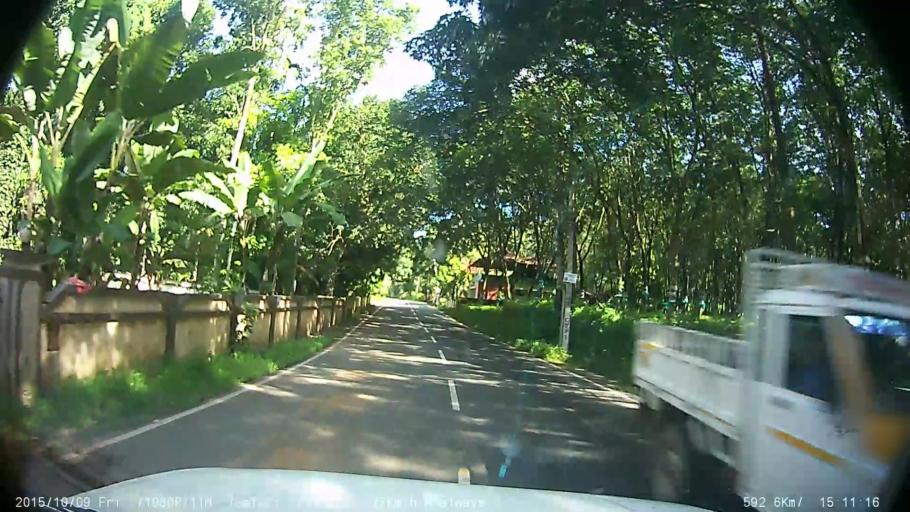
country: IN
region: Kerala
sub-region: Ernakulam
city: Piravam
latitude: 9.8761
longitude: 76.5779
